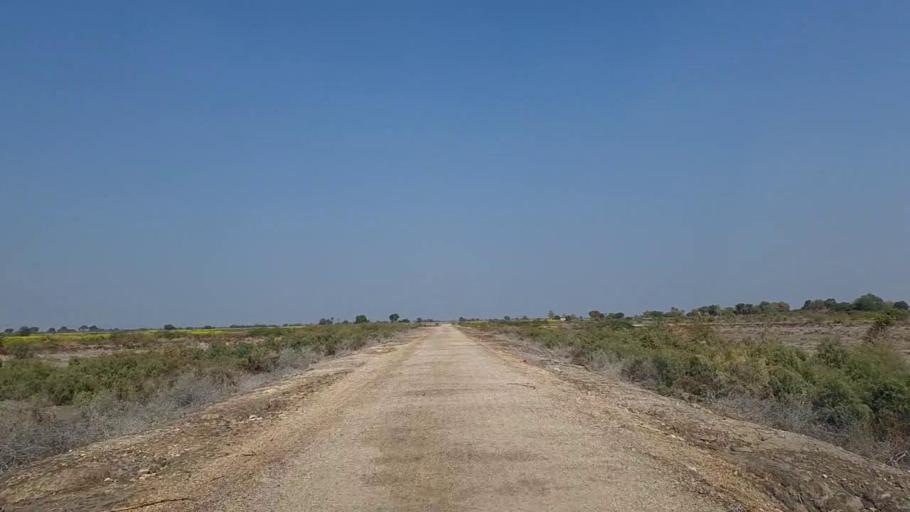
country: PK
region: Sindh
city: Nawabshah
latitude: 26.2909
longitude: 68.4810
